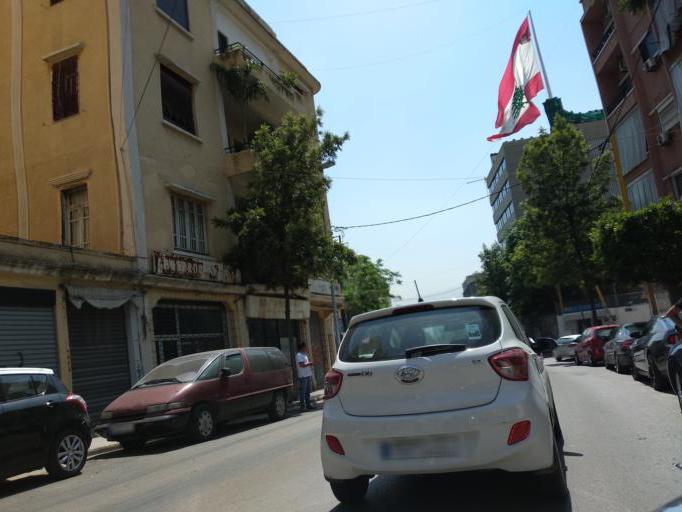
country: LB
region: Mont-Liban
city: Jdaidet el Matn
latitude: 33.8963
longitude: 35.5326
